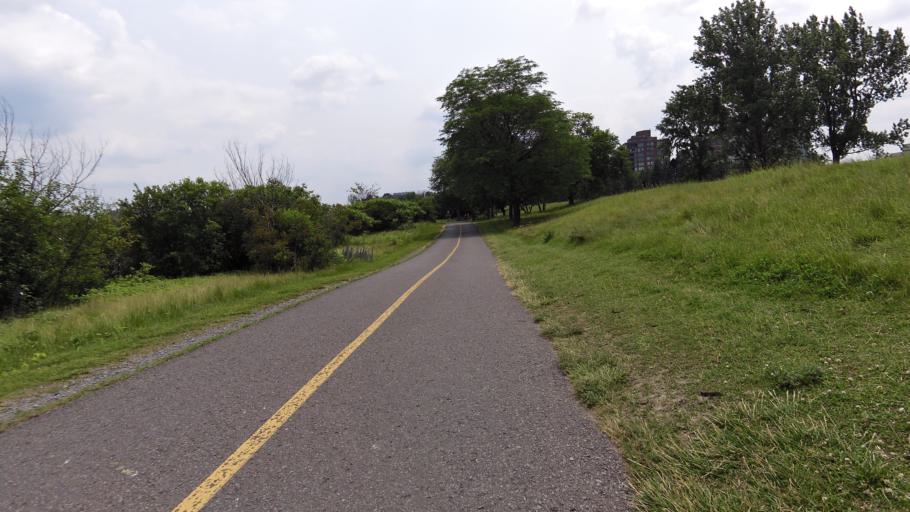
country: CA
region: Ontario
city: Ottawa
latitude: 45.4125
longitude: -75.7344
